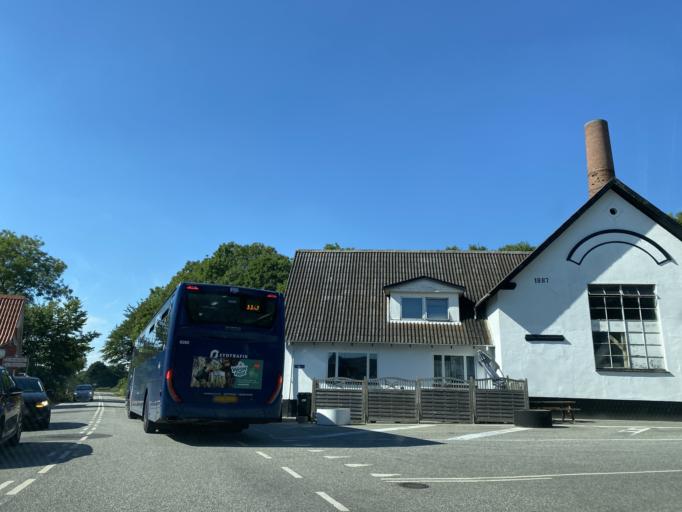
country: DK
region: Central Jutland
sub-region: Hedensted Kommune
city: Torring
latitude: 55.8160
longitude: 9.4605
